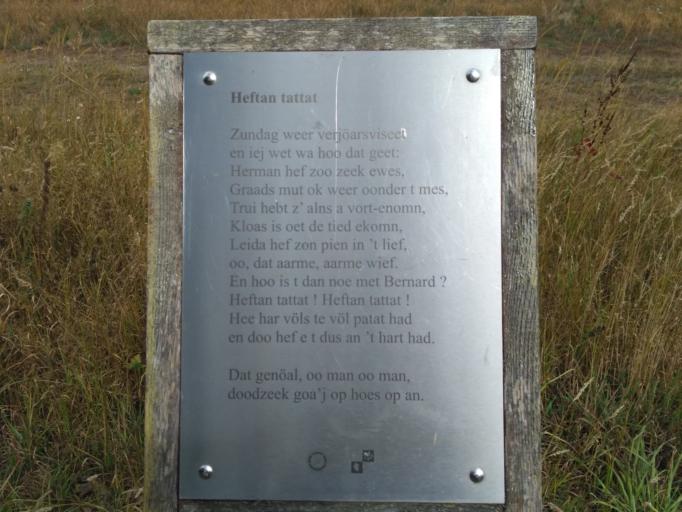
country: NL
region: Overijssel
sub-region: Gemeente Hengelo
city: Hengelo
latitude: 52.2768
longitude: 6.8447
